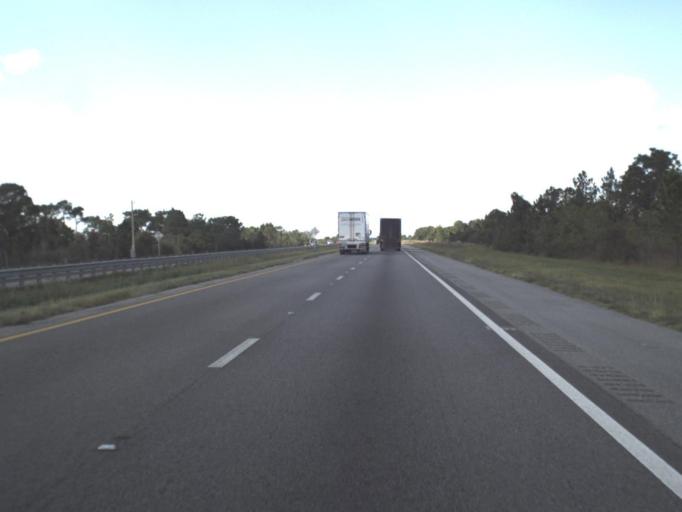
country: US
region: Florida
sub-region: Indian River County
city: Fellsmere
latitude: 27.7849
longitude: -80.9759
